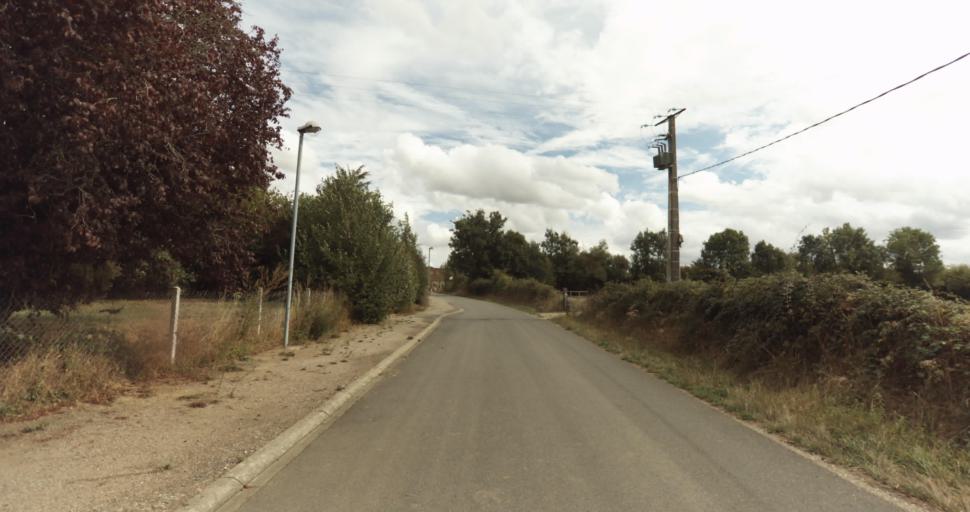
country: FR
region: Lower Normandy
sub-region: Departement de l'Orne
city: Gace
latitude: 48.8901
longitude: 0.3427
